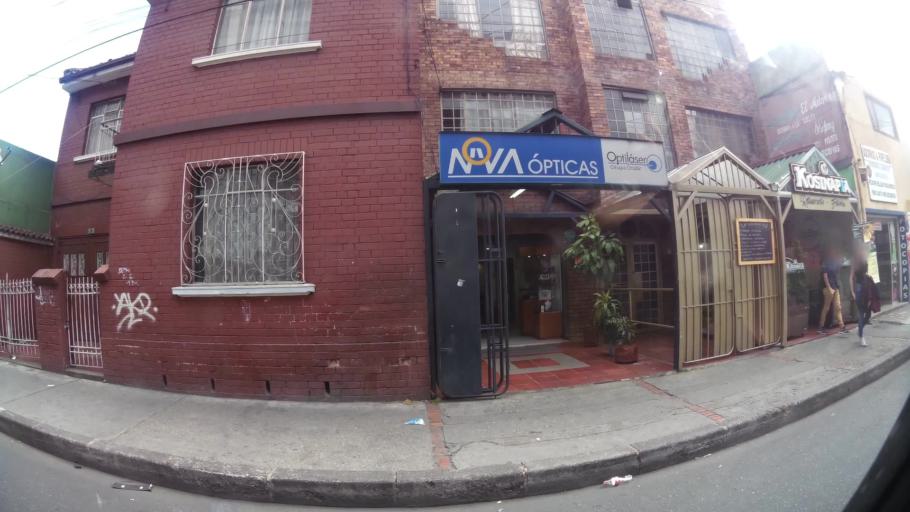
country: CO
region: Bogota D.C.
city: Bogota
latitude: 4.6388
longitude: -74.0685
